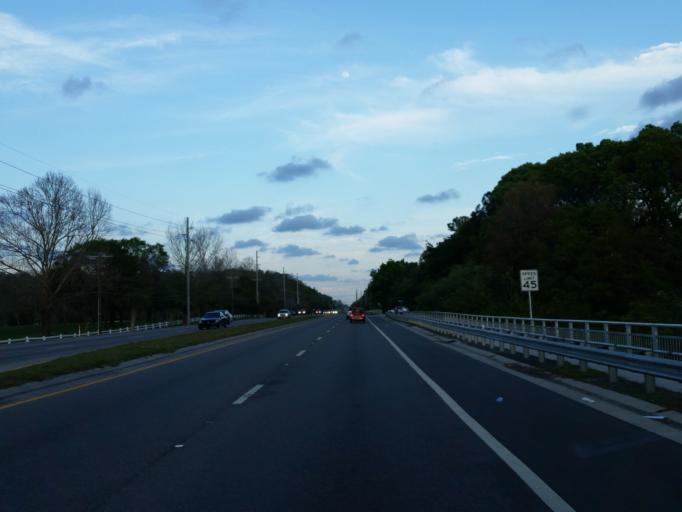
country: US
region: Florida
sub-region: Hillsborough County
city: University
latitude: 28.0690
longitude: -82.4094
